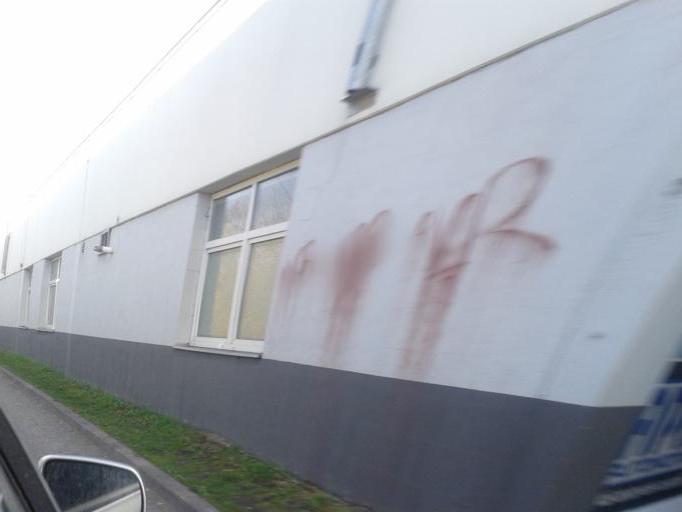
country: CZ
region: Central Bohemia
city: Hostivice
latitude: 50.0537
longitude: 14.2984
